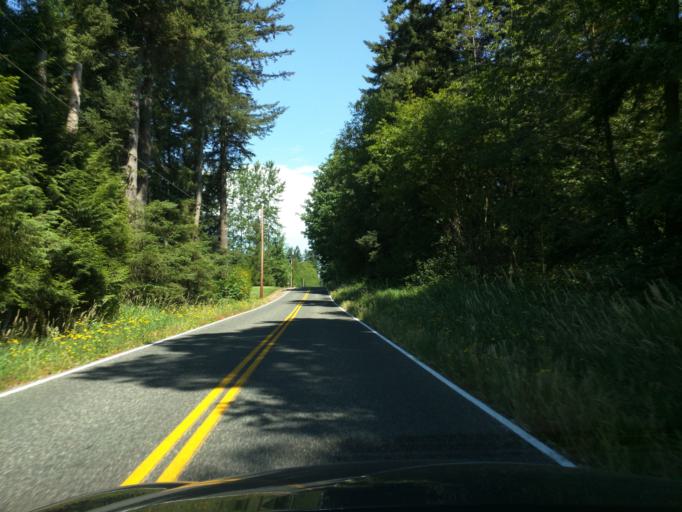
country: CA
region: British Columbia
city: Langley
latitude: 48.9805
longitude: -122.5961
